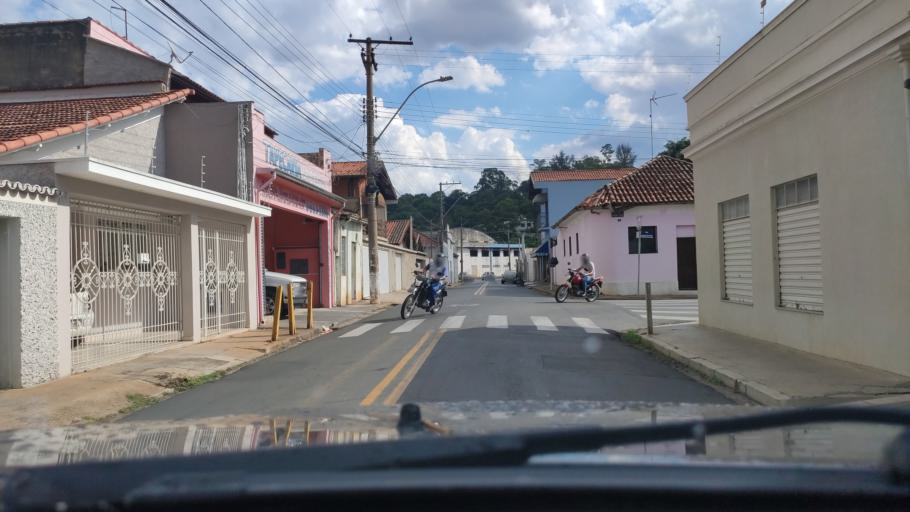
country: BR
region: Sao Paulo
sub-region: Itapira
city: Itapira
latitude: -22.4381
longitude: -46.8172
